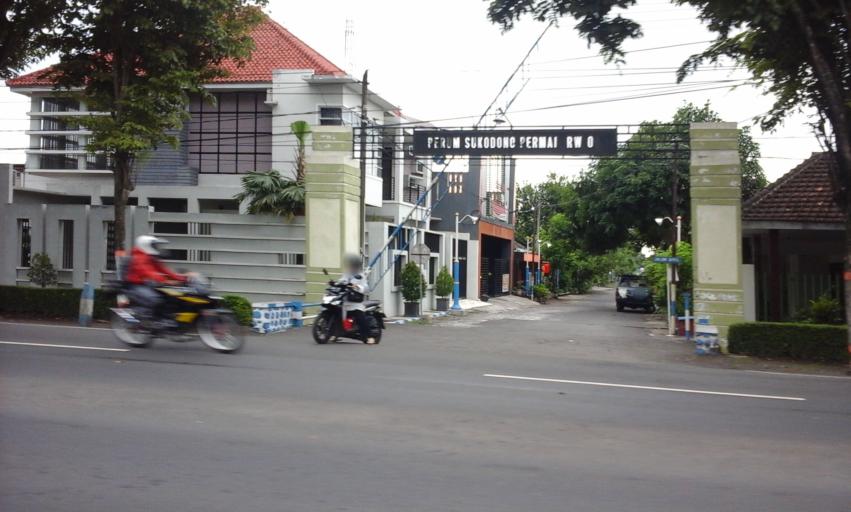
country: ID
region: East Java
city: Sukodono
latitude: -8.1012
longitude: 113.2333
